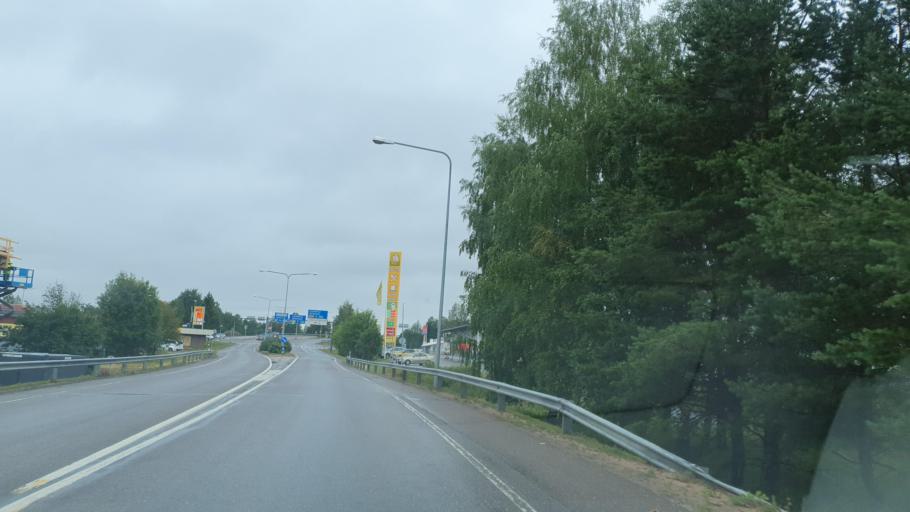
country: FI
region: Lapland
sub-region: Itae-Lappi
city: Kemijaervi
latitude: 66.7170
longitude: 27.4313
